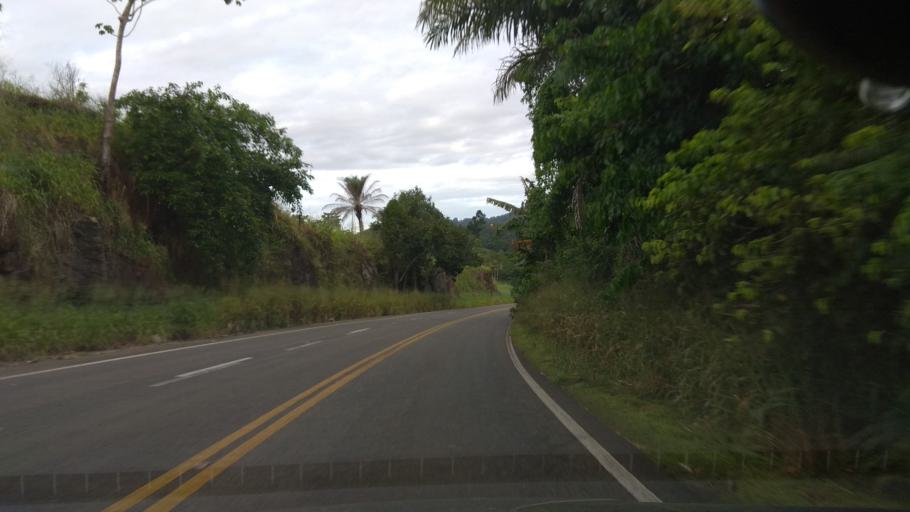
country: BR
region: Bahia
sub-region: Ubaitaba
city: Ubaitaba
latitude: -14.2465
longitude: -39.3592
